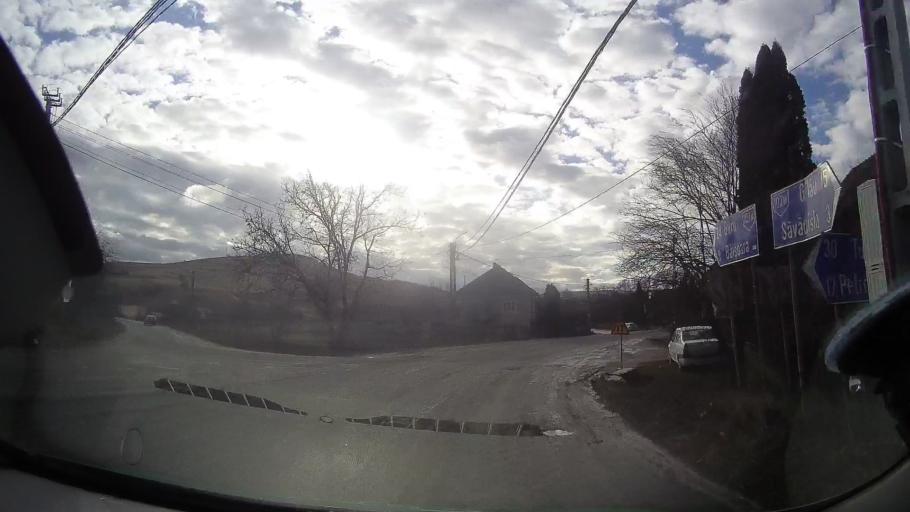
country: RO
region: Cluj
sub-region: Comuna Savadisla
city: Savadisla
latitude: 46.6424
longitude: 23.4618
